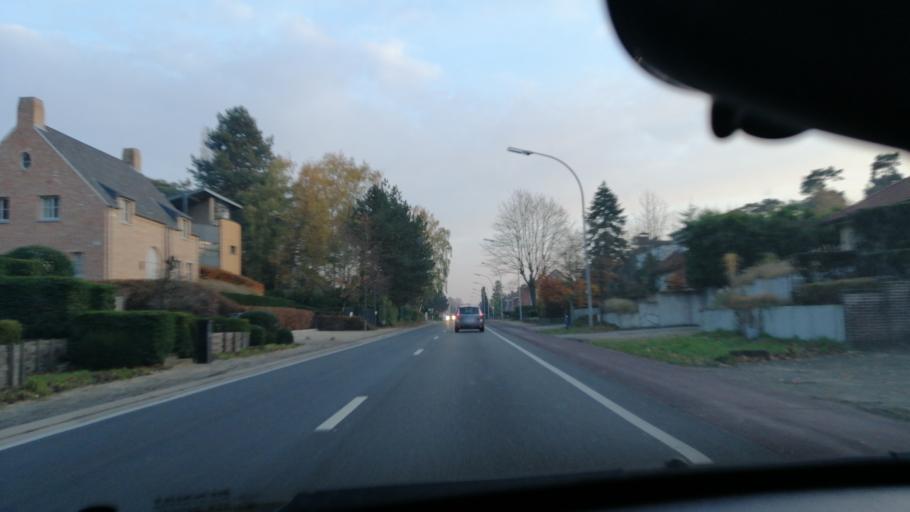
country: BE
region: Flanders
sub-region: Provincie Antwerpen
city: Herentals
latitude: 51.1933
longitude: 4.8288
